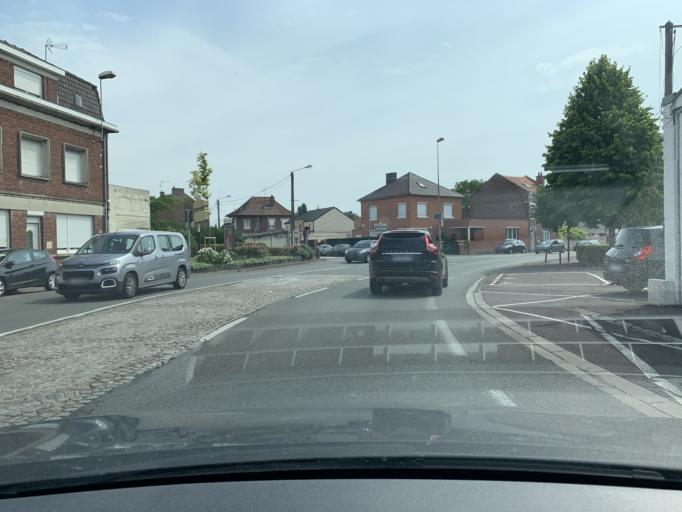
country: FR
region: Nord-Pas-de-Calais
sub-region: Departement du Nord
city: Douai
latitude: 50.3631
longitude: 3.0674
